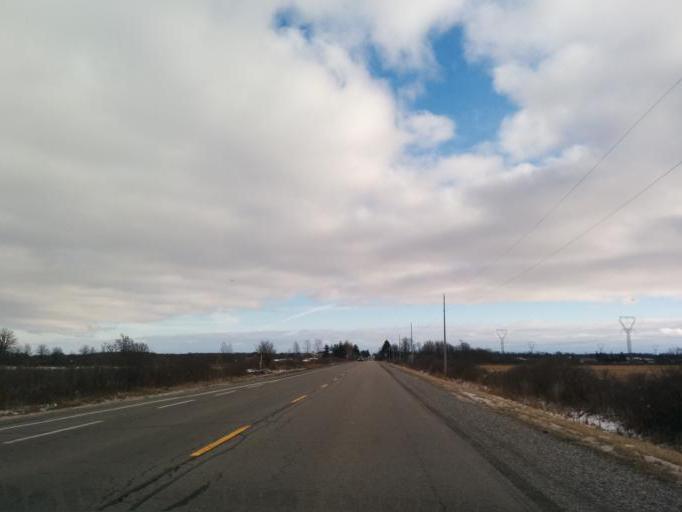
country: CA
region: Ontario
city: Brantford
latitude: 42.9824
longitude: -80.1073
